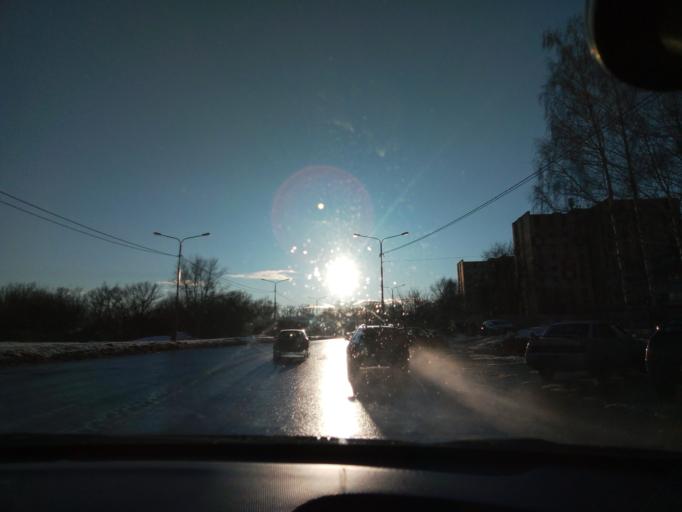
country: RU
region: Chuvashia
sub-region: Cheboksarskiy Rayon
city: Cheboksary
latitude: 56.1375
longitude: 47.2065
